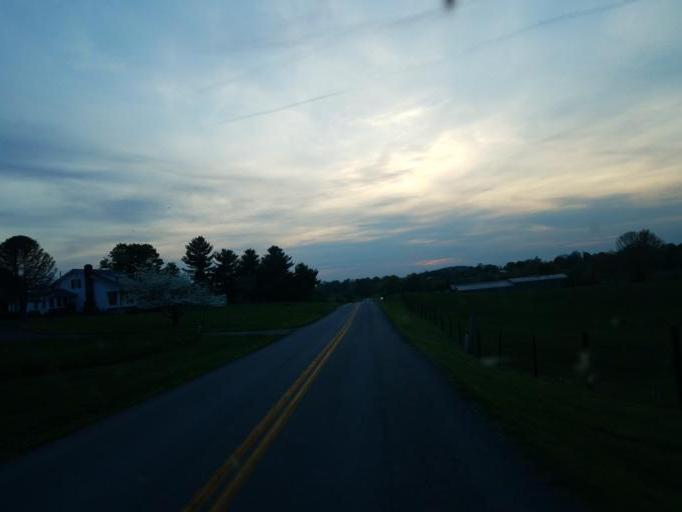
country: US
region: Kentucky
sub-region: Hart County
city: Munfordville
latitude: 37.2506
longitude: -85.7748
